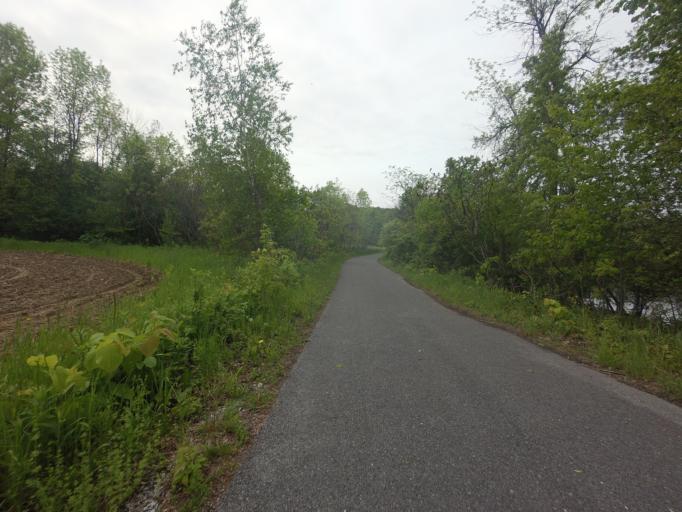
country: US
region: New York
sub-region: Jefferson County
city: Black River
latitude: 43.9940
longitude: -75.8221
